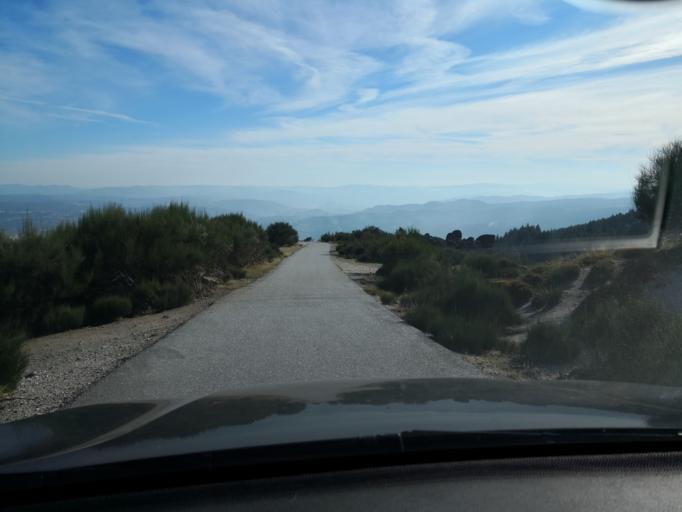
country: PT
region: Vila Real
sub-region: Vila Real
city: Vila Real
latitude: 41.3439
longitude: -7.7639
